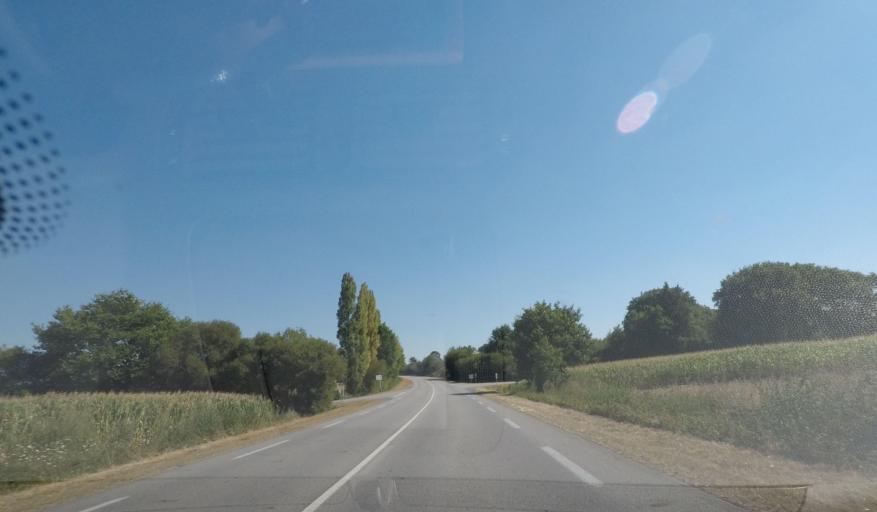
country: FR
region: Brittany
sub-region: Departement du Morbihan
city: Questembert
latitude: 47.6401
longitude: -2.4250
